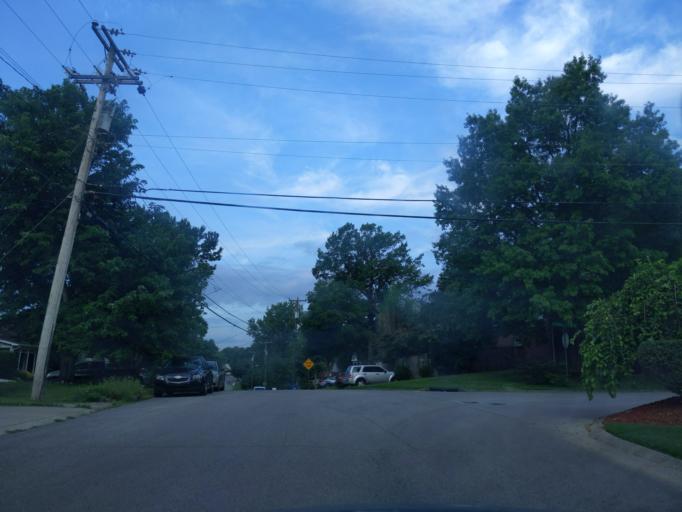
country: US
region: Tennessee
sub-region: Wilson County
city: Green Hill
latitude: 36.1844
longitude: -86.5988
